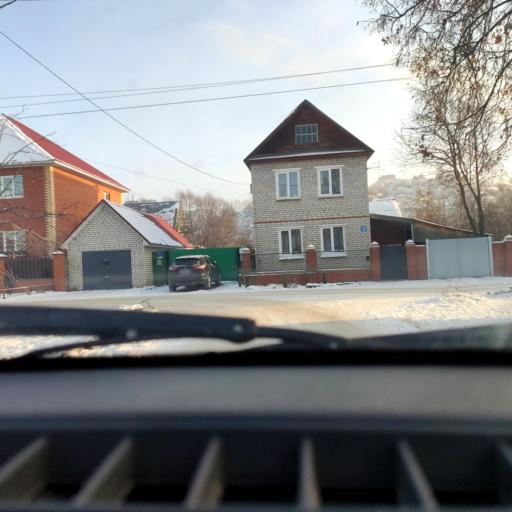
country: RU
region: Bashkortostan
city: Ufa
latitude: 54.7382
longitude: 55.9163
